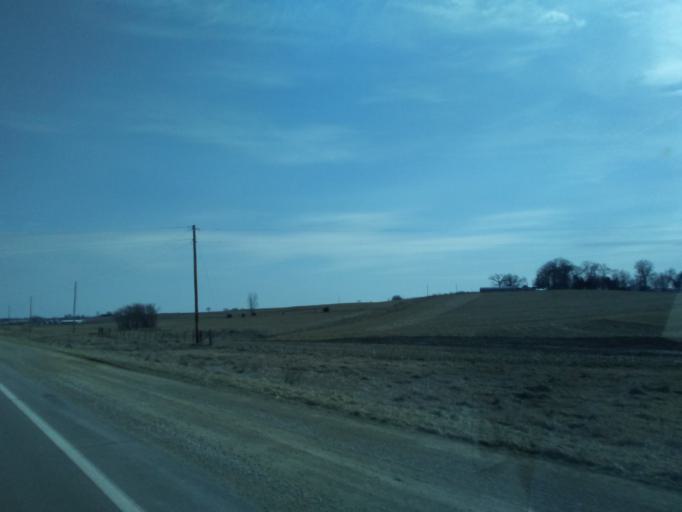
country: US
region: Iowa
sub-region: Winneshiek County
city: Decorah
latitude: 43.4038
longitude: -91.8504
